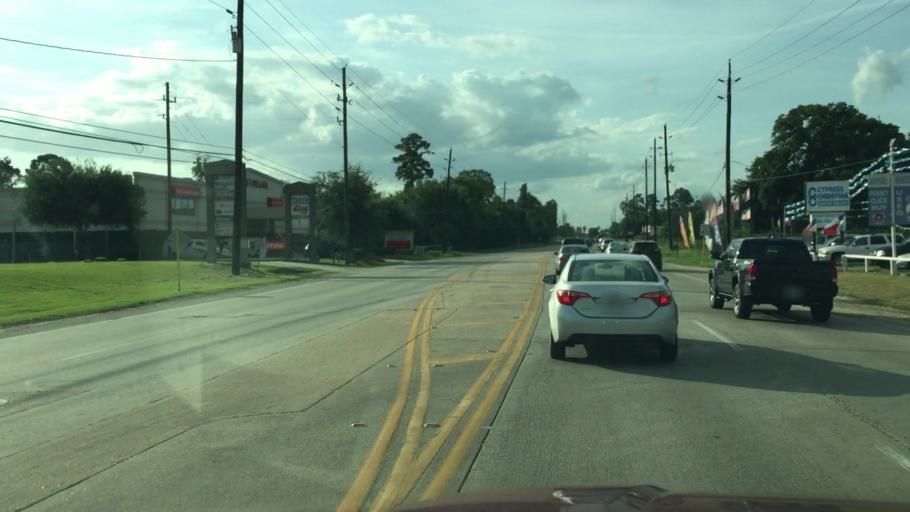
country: US
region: Texas
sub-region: Harris County
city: Hudson
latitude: 29.9996
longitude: -95.5069
